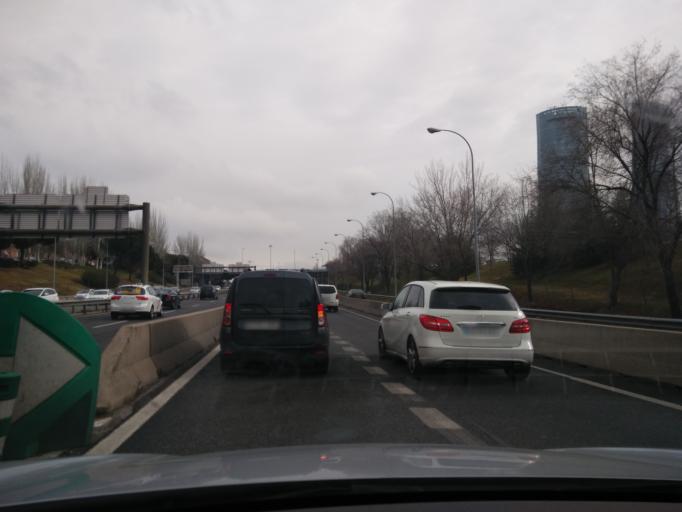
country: ES
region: Madrid
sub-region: Provincia de Madrid
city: Pinar de Chamartin
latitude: 40.4849
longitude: -3.6923
